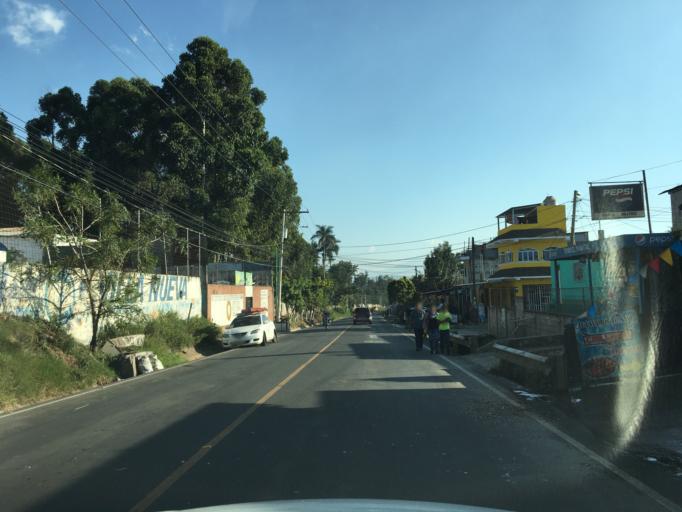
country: GT
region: Guatemala
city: Villa Nueva
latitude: 14.5408
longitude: -90.6156
